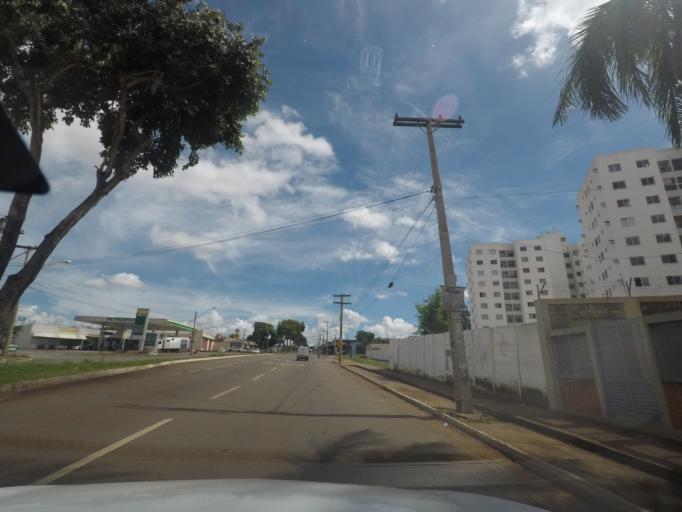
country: BR
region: Goias
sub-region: Goiania
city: Goiania
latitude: -16.7327
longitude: -49.3257
